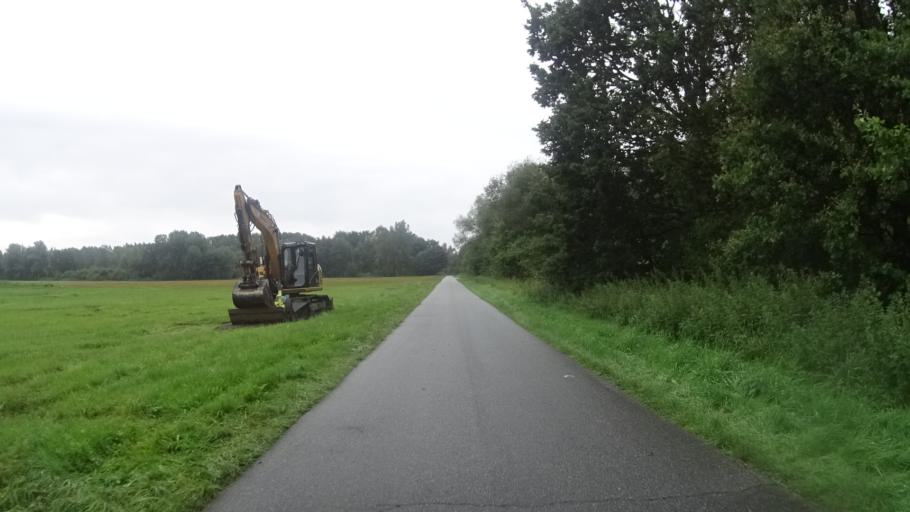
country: DE
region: Schleswig-Holstein
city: Siebeneichen
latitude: 53.4956
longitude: 10.6222
